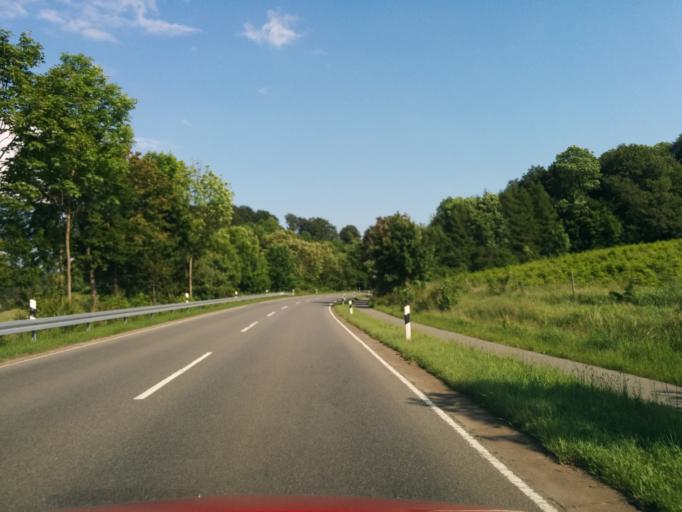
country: DE
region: Lower Saxony
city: Bad Lauterberg im Harz
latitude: 51.6065
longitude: 10.4470
